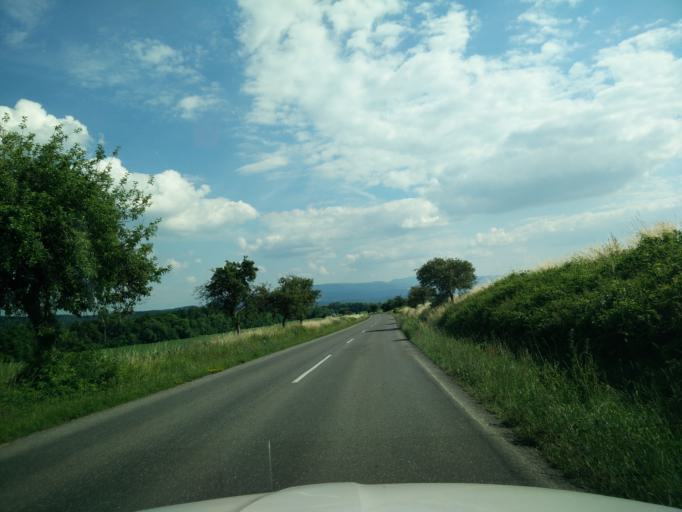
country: SK
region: Nitriansky
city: Prievidza
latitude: 48.8628
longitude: 18.6408
